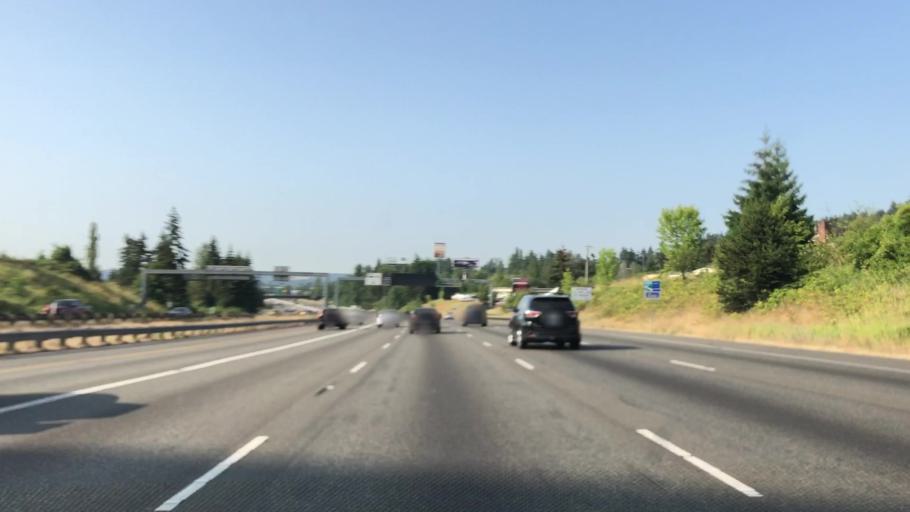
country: US
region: Washington
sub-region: Pierce County
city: Milton
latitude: 47.2582
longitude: -122.3232
